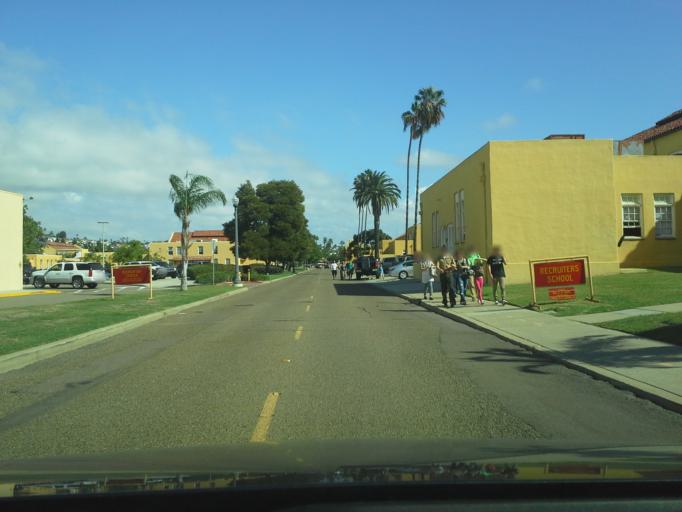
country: US
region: California
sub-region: San Diego County
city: San Diego
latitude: 32.7436
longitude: -117.2007
